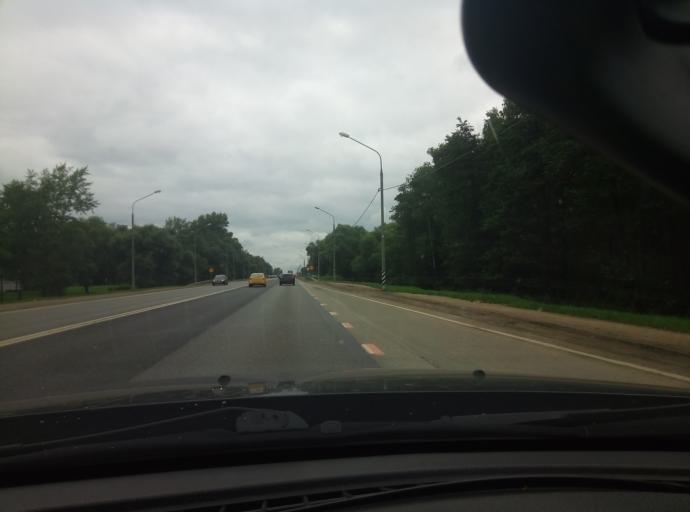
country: RU
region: Kaluga
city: Obninsk
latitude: 55.0971
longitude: 36.6377
